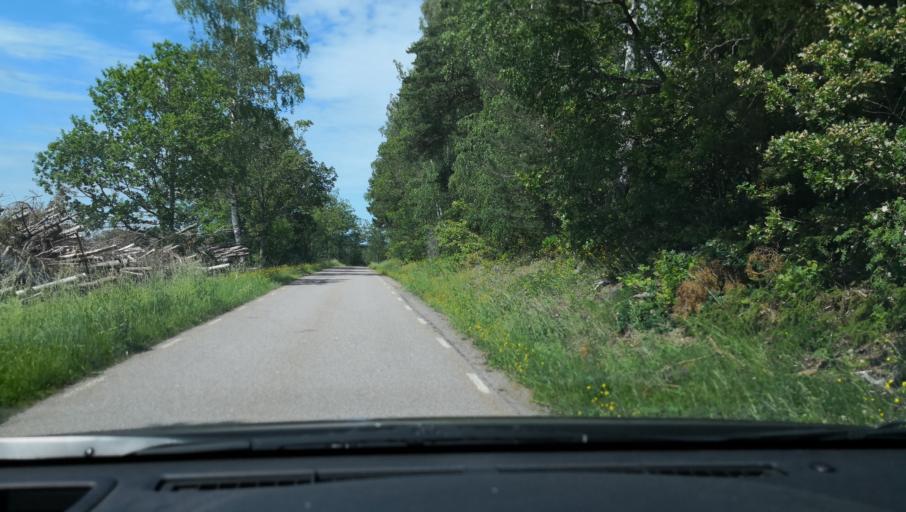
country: SE
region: Stockholm
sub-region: Sigtuna Kommun
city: Sigtuna
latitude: 59.6961
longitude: 17.6430
